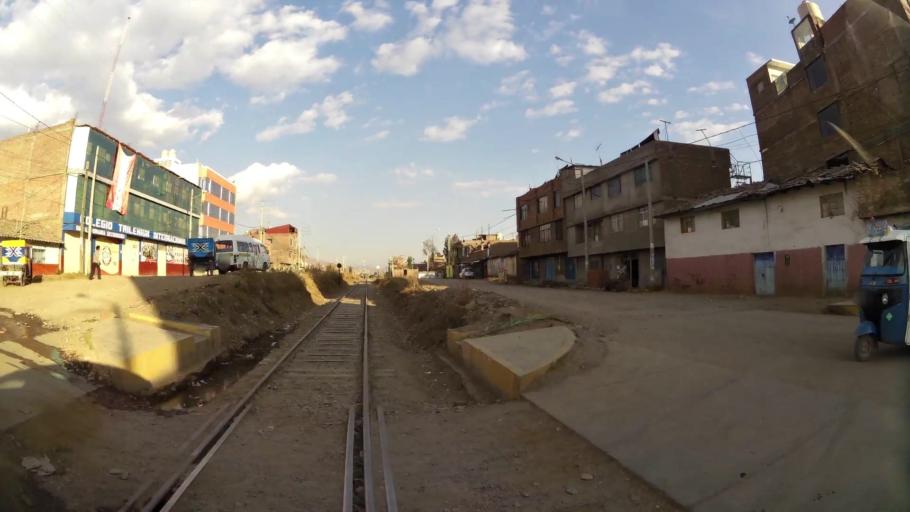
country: PE
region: Junin
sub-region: Provincia de Huancayo
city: Pilcomay
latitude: -12.0295
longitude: -75.2323
